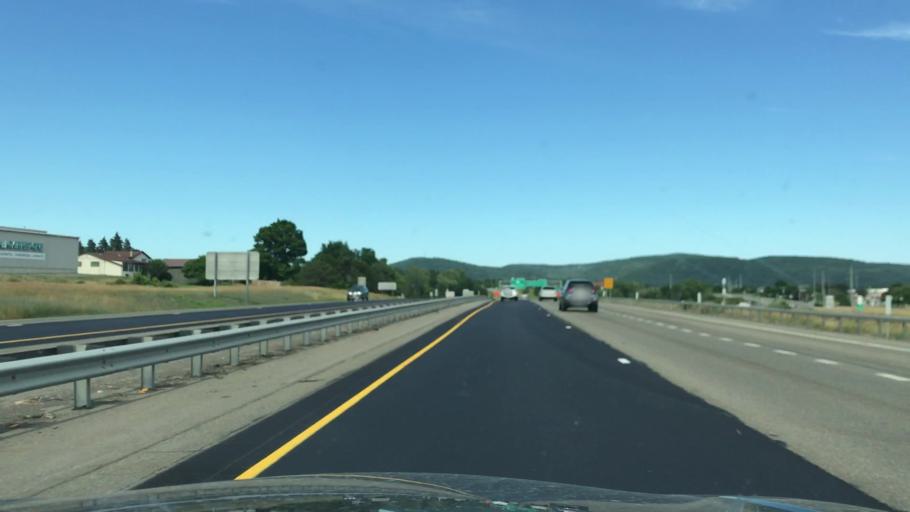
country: US
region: New York
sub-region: Chemung County
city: Horseheads
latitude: 42.1605
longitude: -76.8579
